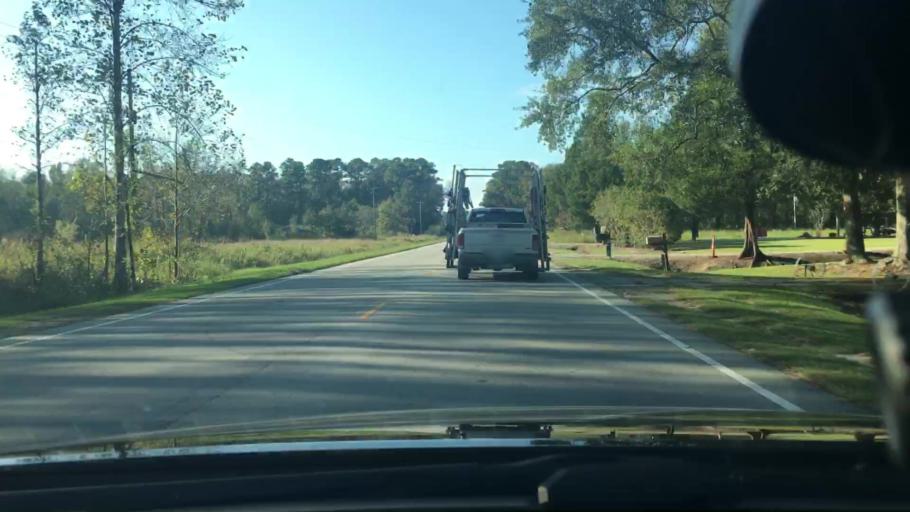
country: US
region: North Carolina
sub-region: Craven County
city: Vanceboro
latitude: 35.2664
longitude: -77.1072
